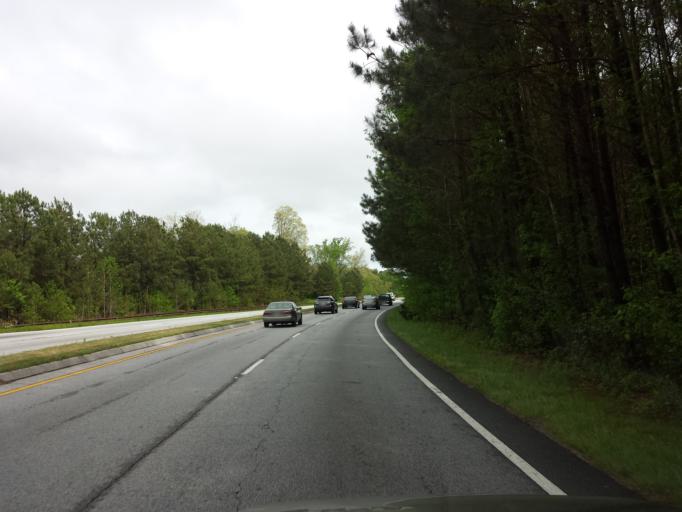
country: US
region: Georgia
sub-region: Cobb County
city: Mableton
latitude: 33.8560
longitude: -84.5631
